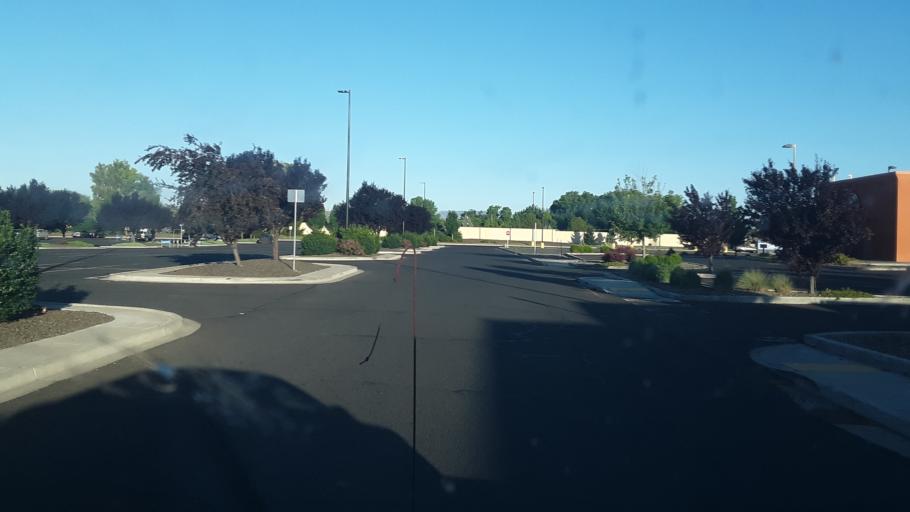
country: US
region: Washington
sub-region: Yakima County
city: West Valley
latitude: 46.5851
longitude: -120.5969
